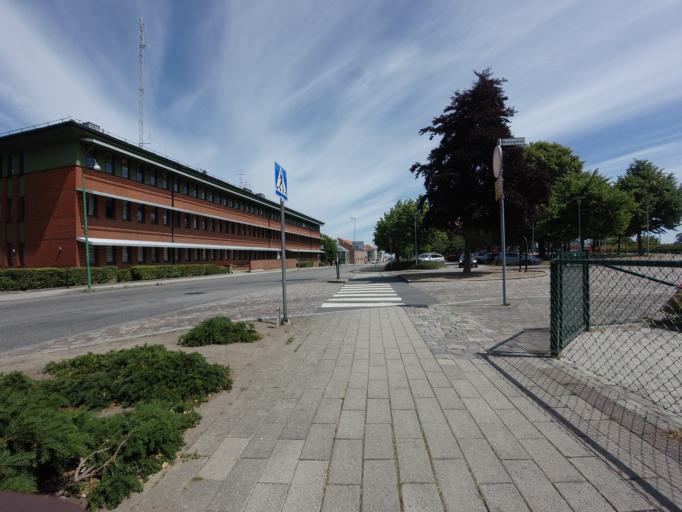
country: SE
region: Skane
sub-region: Simrishamns Kommun
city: Simrishamn
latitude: 55.5541
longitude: 14.3513
